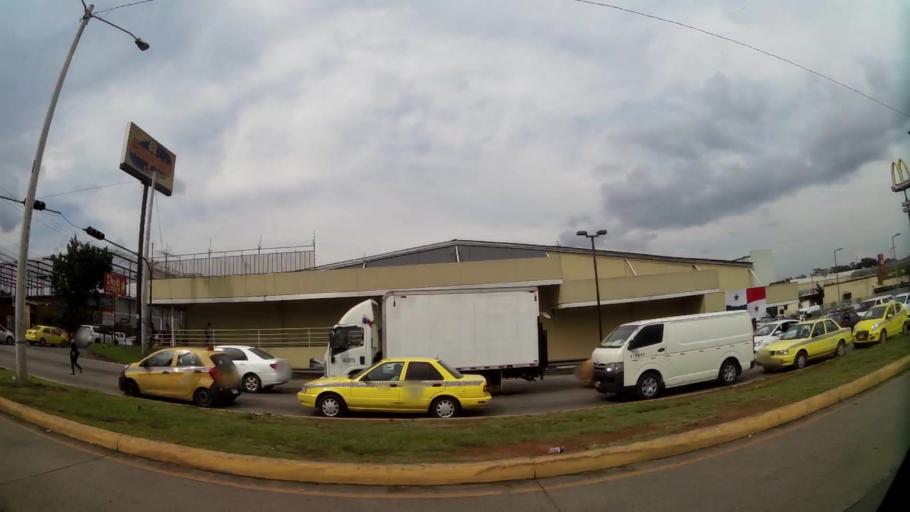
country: PA
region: Panama
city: Tocumen
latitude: 9.1035
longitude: -79.3714
